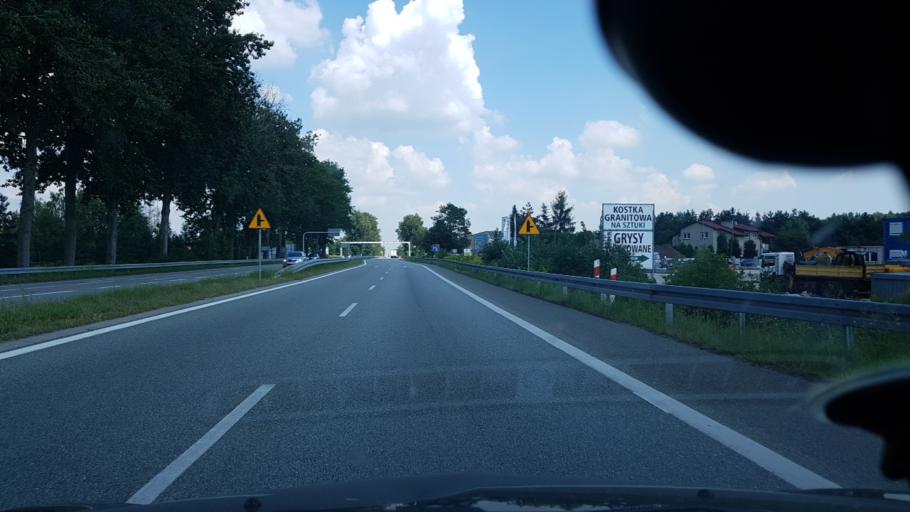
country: PL
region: Silesian Voivodeship
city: Gardawice
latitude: 50.0880
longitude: 18.7581
